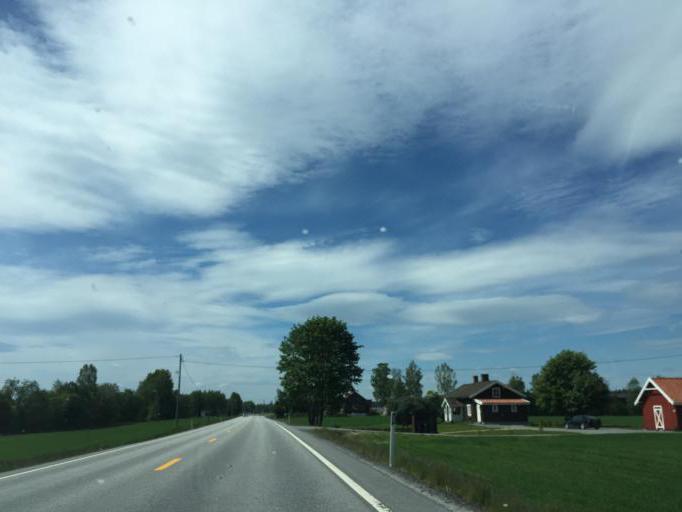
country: NO
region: Hedmark
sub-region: Sor-Odal
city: Skarnes
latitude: 60.2066
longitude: 11.6004
